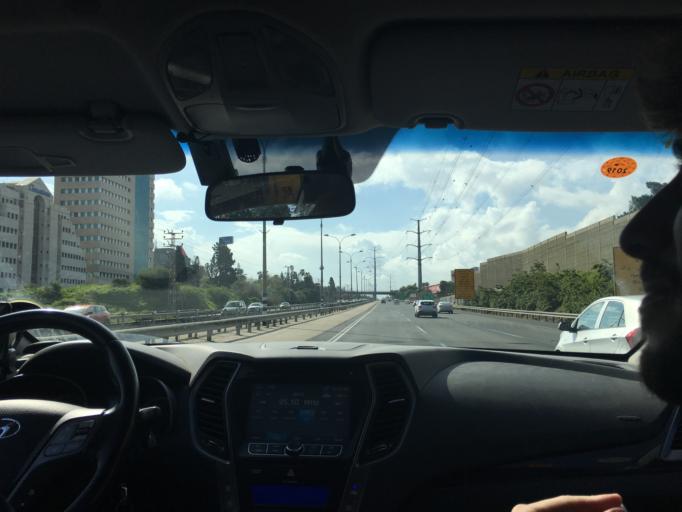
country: IL
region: Tel Aviv
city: Giv`at Shemu'el
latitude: 32.0814
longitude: 34.8450
